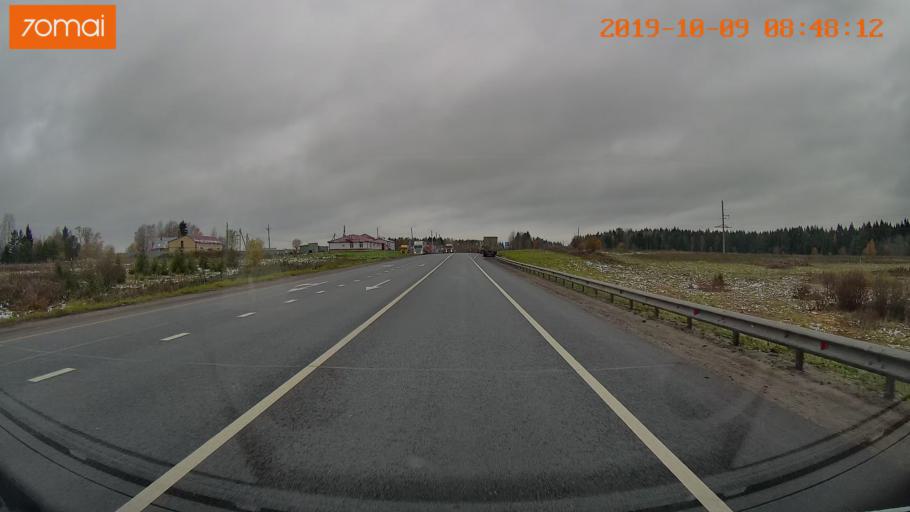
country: RU
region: Vologda
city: Vologda
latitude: 59.0715
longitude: 40.0298
